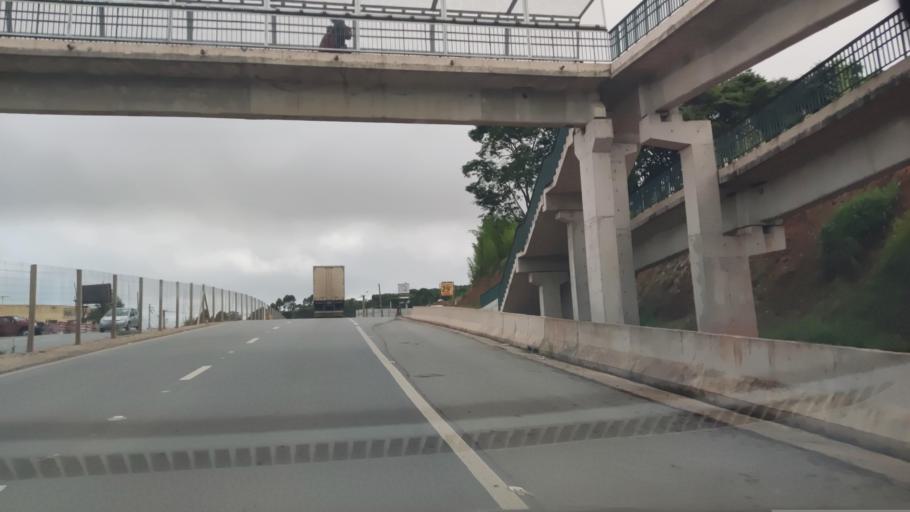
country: BR
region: Sao Paulo
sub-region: Vargem Grande Paulista
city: Vargem Grande Paulista
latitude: -23.6246
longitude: -47.0493
